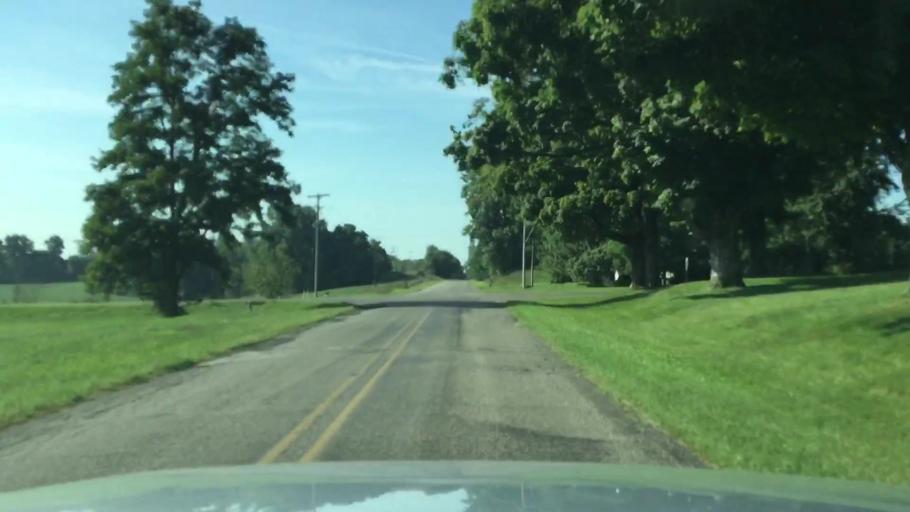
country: US
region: Michigan
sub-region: Lenawee County
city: Hudson
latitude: 41.8845
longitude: -84.4202
